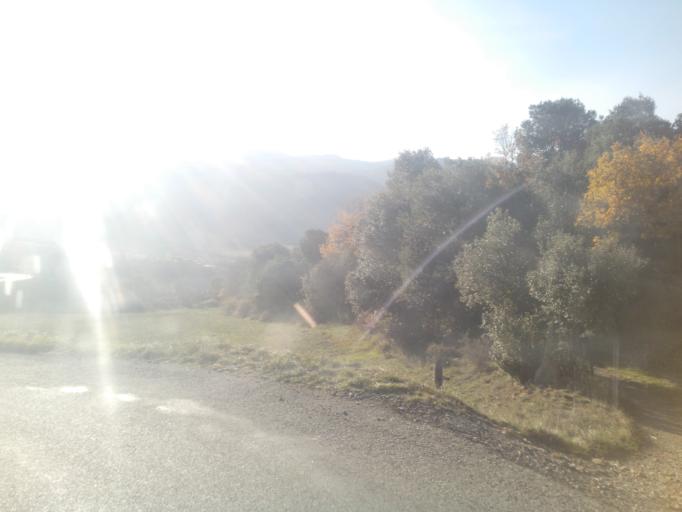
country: FR
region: Languedoc-Roussillon
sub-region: Departement de l'Aude
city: Couiza
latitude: 42.8794
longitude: 2.3597
